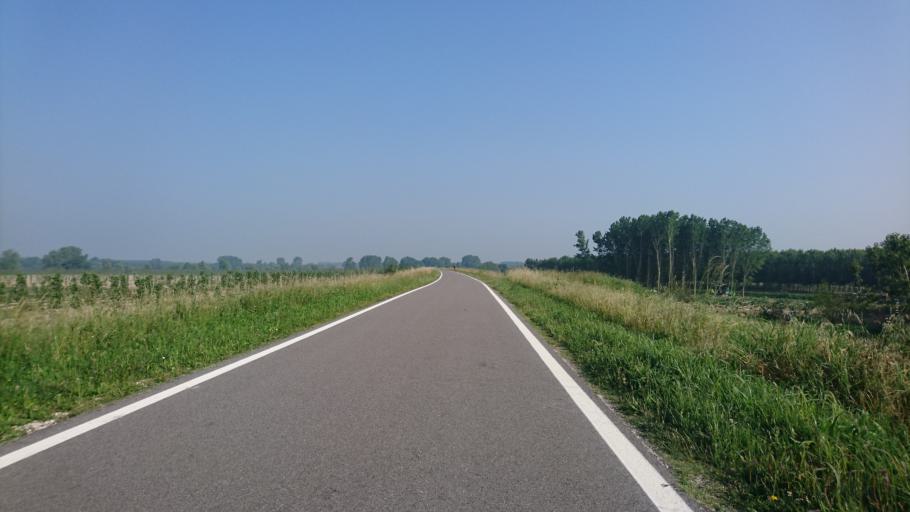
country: IT
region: Veneto
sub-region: Provincia di Rovigo
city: Castelnovo Bariano
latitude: 45.0284
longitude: 11.2711
